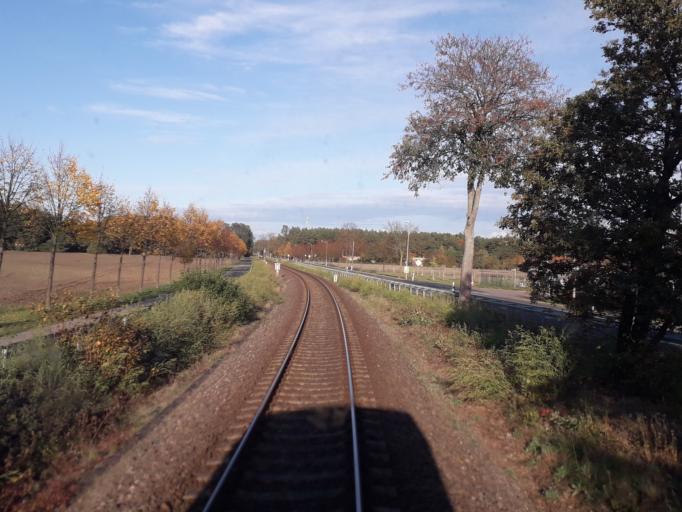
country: DE
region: Brandenburg
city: Weisen
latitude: 53.0278
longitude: 11.7948
